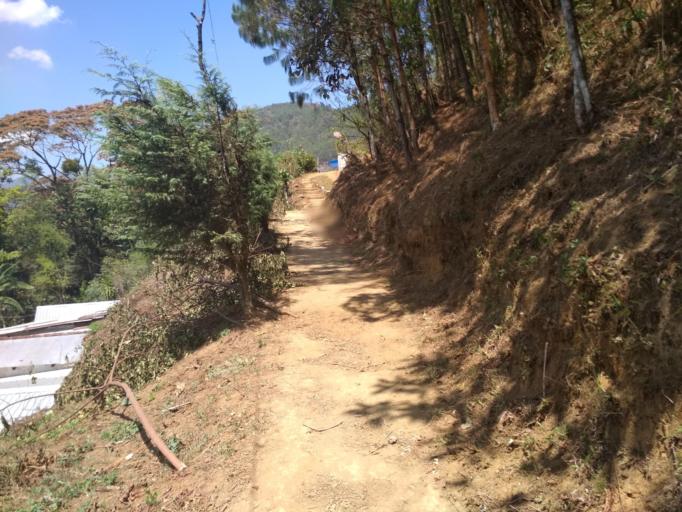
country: MX
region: Veracruz
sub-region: Tlilapan
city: Tonalixco
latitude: 18.7807
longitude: -97.0760
